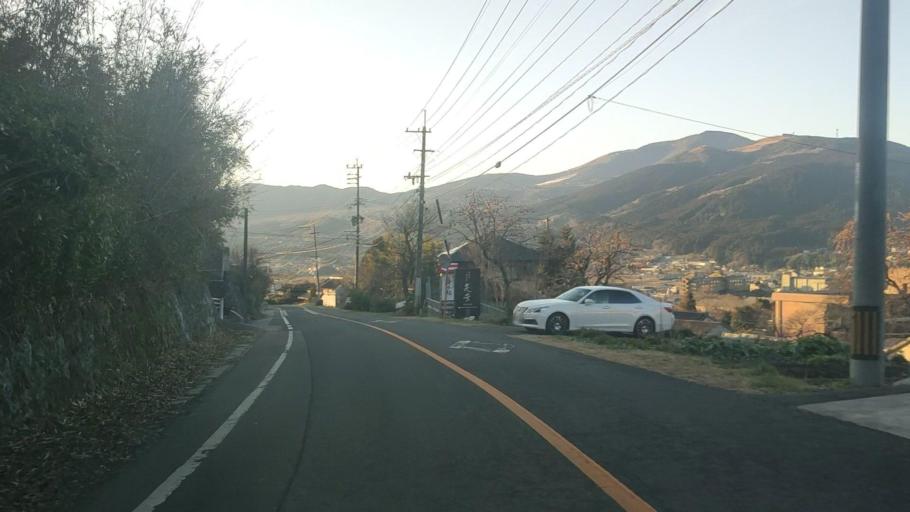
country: JP
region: Oita
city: Beppu
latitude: 33.2548
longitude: 131.3635
